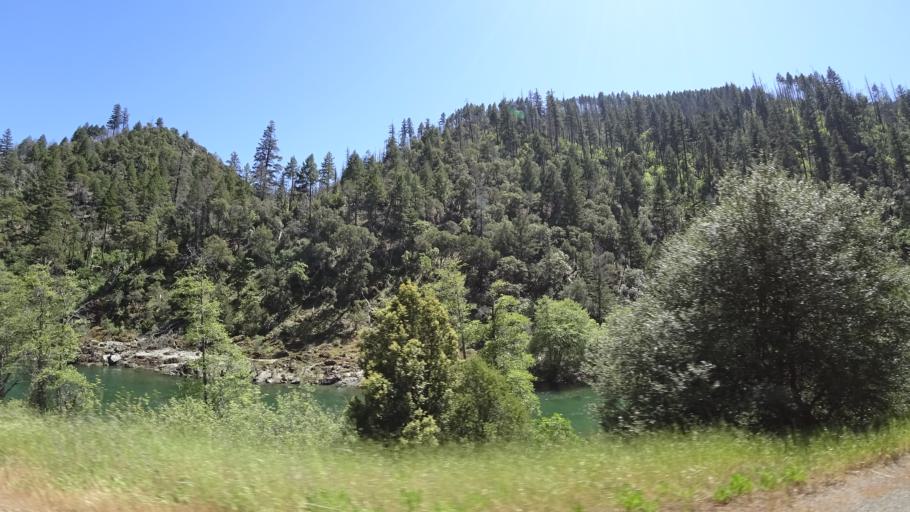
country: US
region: California
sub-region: Trinity County
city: Hayfork
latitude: 40.7665
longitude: -123.3009
